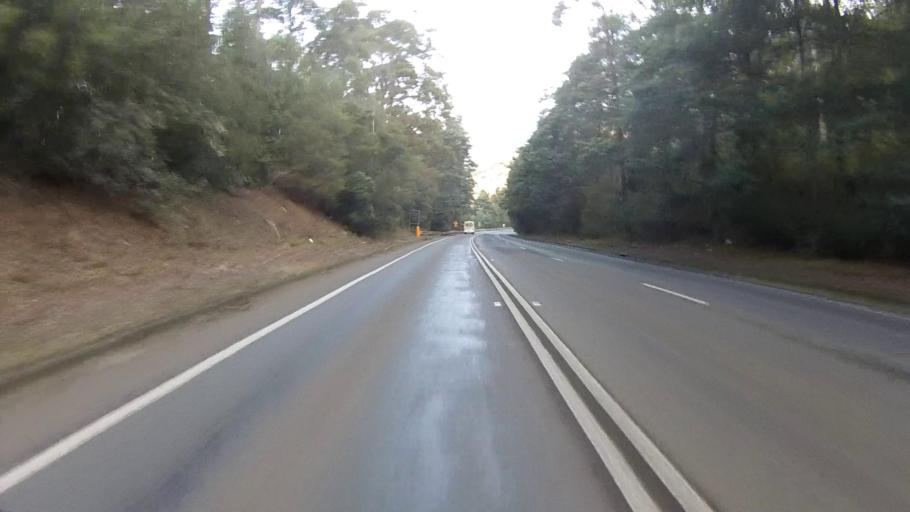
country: AU
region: Tasmania
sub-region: Sorell
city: Sorell
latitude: -43.0081
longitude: 147.9267
